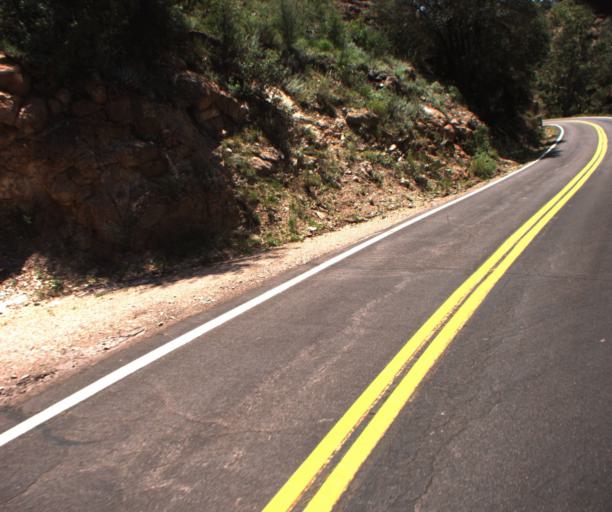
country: US
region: Arizona
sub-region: Greenlee County
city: Morenci
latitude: 33.1632
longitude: -109.3701
